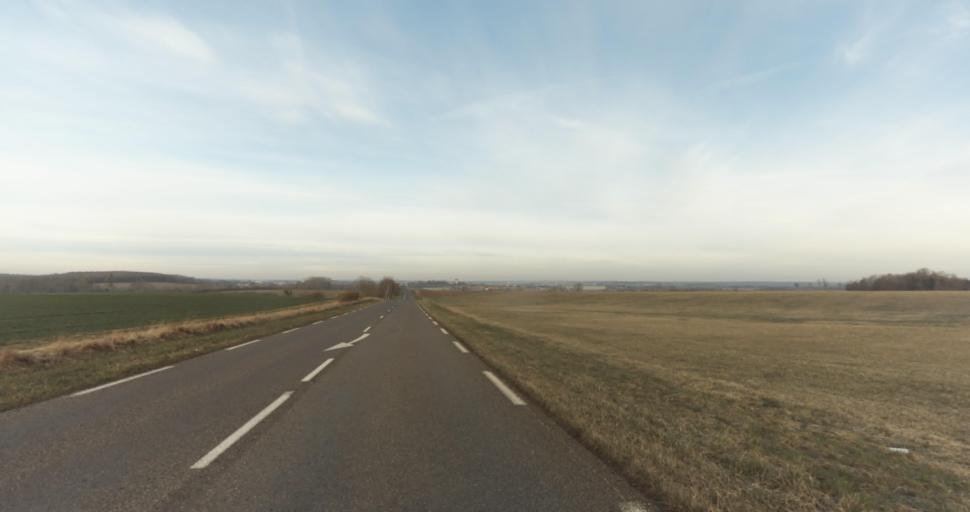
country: FR
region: Lorraine
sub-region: Departement de Meurthe-et-Moselle
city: Doncourt-les-Conflans
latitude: 49.1472
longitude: 5.9203
